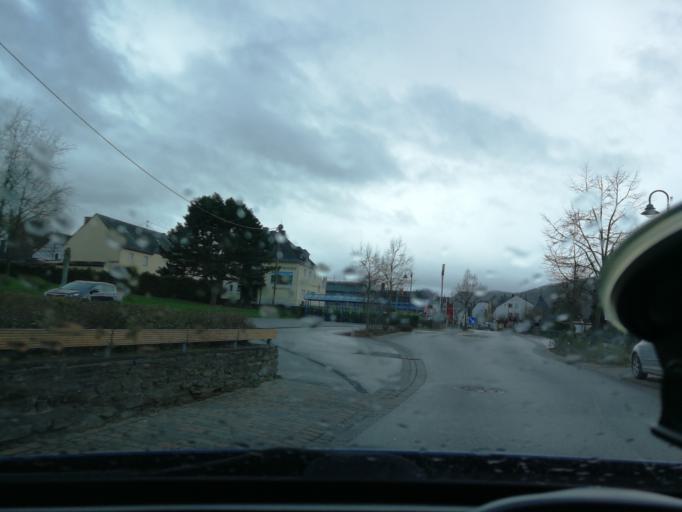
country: DE
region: Rheinland-Pfalz
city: Neumagen-Dhron
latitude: 49.8589
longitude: 6.8972
